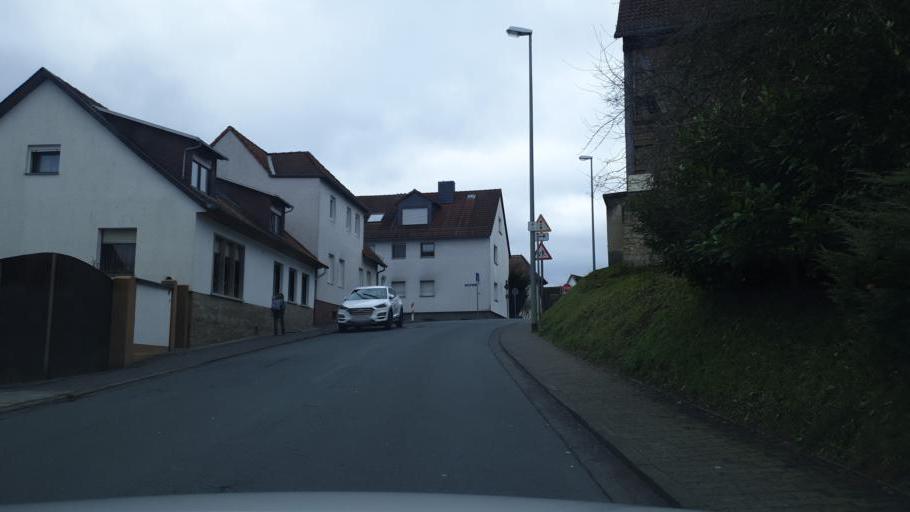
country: DE
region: Hesse
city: Eppstein
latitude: 50.1410
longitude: 8.3568
